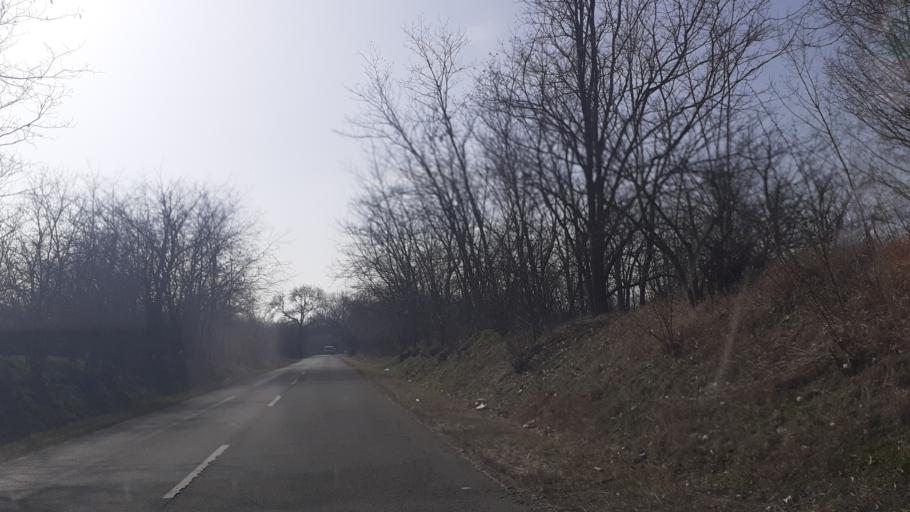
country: HU
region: Pest
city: Orkeny
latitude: 47.0918
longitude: 19.3823
